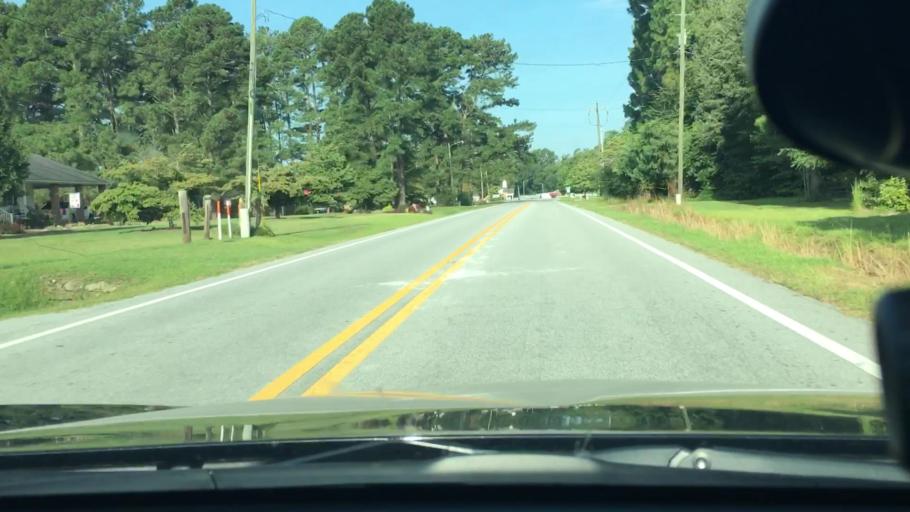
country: US
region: North Carolina
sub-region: Pitt County
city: Farmville
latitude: 35.6960
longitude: -77.5059
